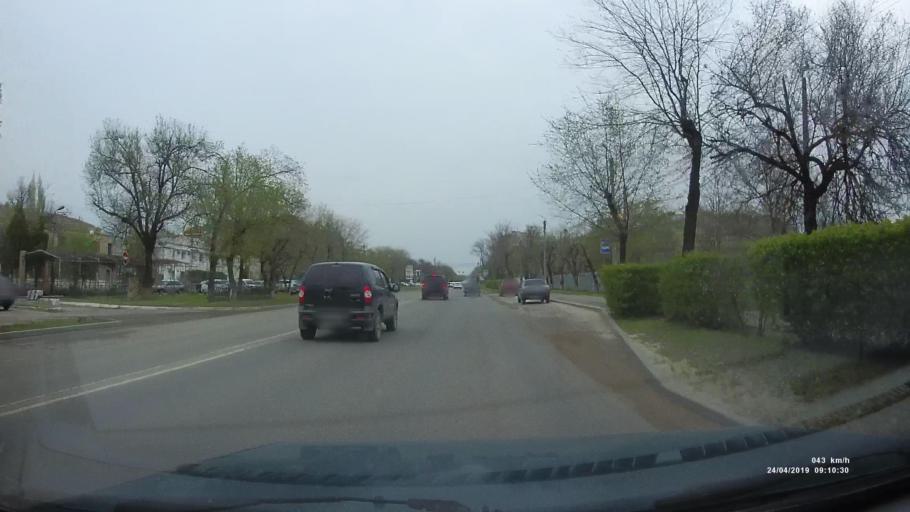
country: RU
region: Kalmykiya
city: Elista
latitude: 46.3099
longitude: 44.2787
